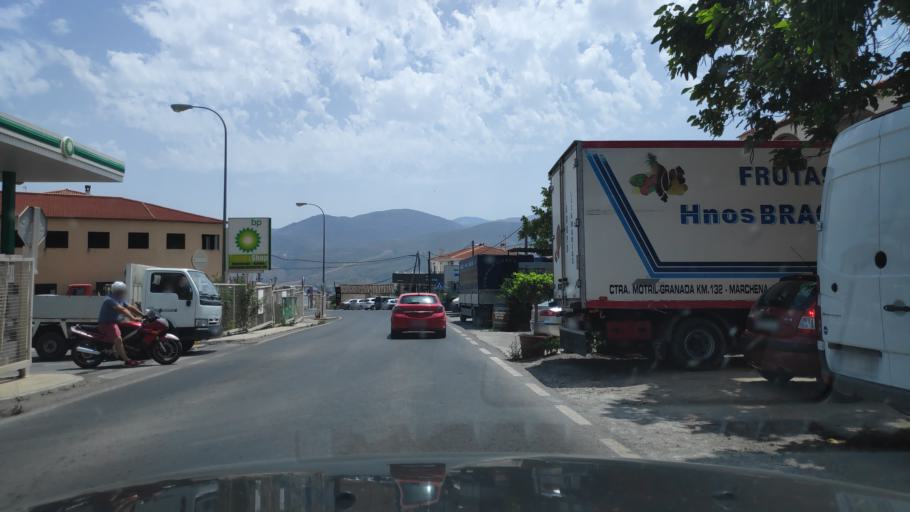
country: ES
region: Andalusia
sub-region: Provincia de Granada
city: Orjiva
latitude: 36.9014
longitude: -3.4300
